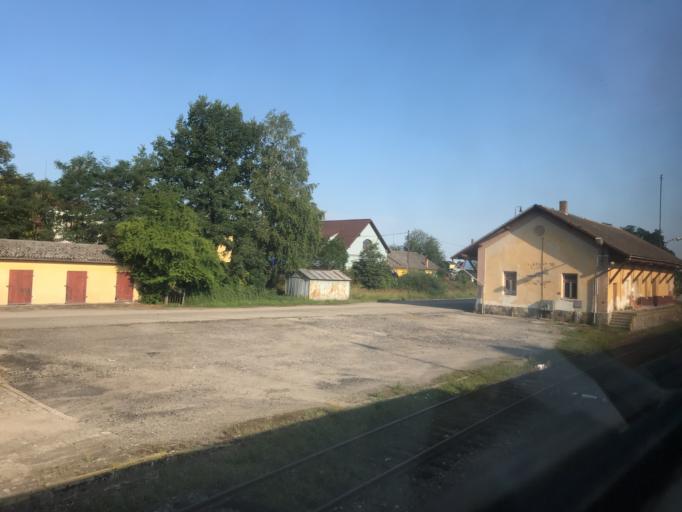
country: CZ
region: Jihocesky
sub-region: Okres Jindrichuv Hradec
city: Trebon
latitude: 49.0157
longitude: 14.7604
